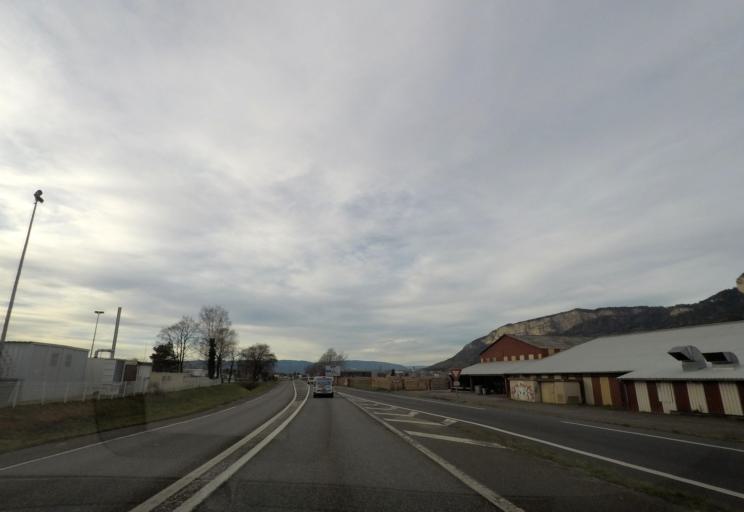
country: FR
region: Rhone-Alpes
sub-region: Departement de la Haute-Savoie
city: Ayse
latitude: 46.0708
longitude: 6.4296
